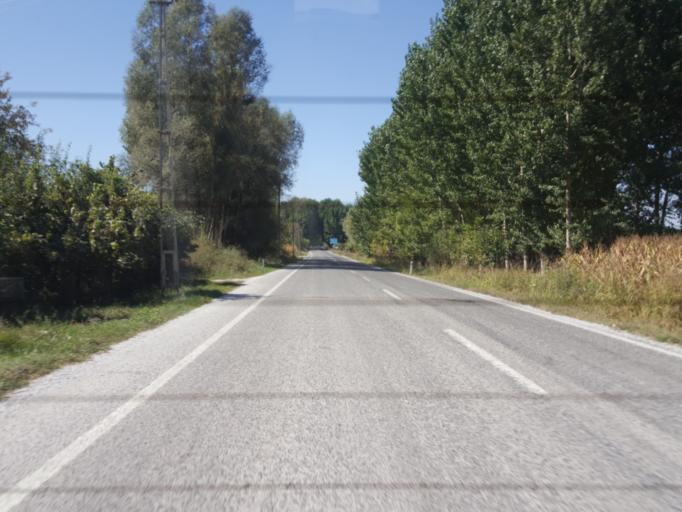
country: TR
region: Tokat
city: Pazar
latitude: 40.2727
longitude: 36.2568
